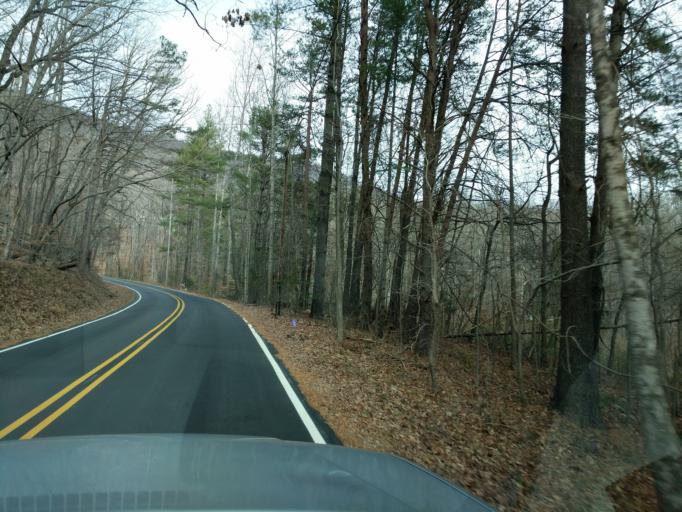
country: US
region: North Carolina
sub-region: Polk County
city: Columbus
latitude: 35.2561
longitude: -82.2319
